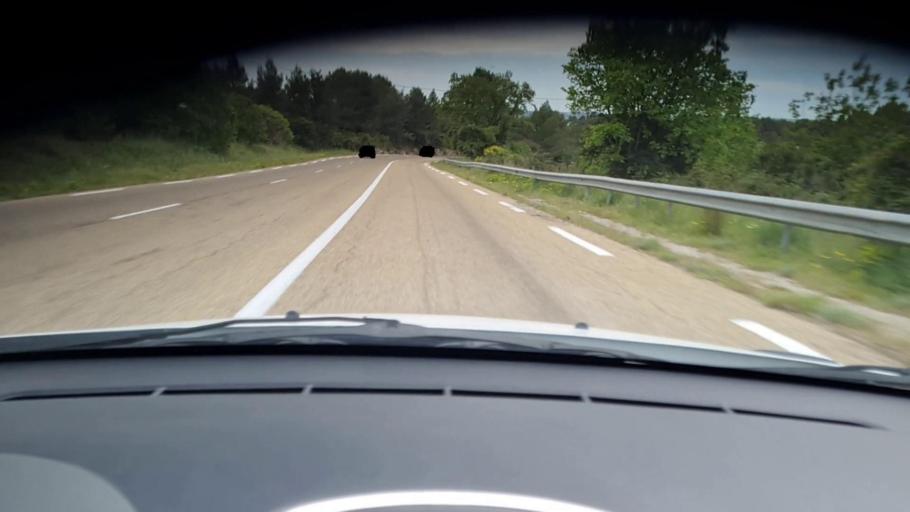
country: FR
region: Languedoc-Roussillon
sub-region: Departement du Gard
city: Nimes
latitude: 43.8705
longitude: 4.3766
